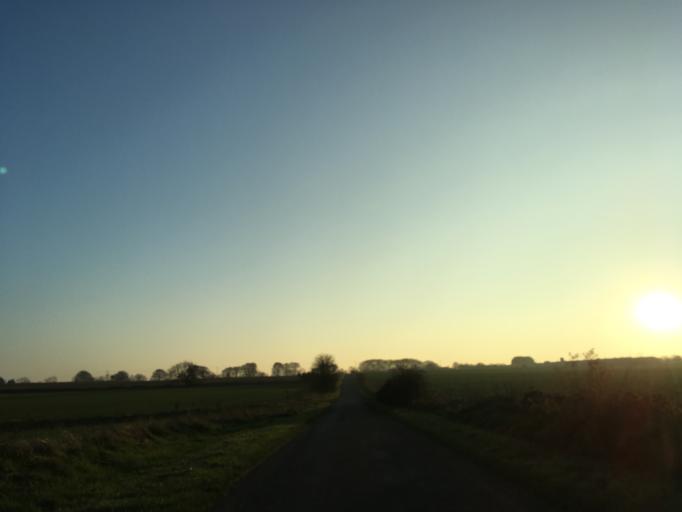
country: GB
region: England
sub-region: South Gloucestershire
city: Marshfield
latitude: 51.4695
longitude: -2.2979
